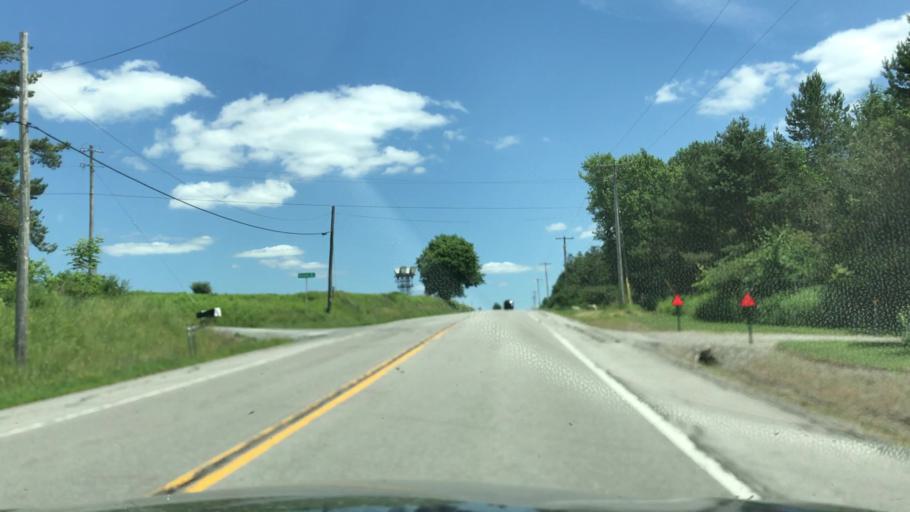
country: US
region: New York
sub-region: Wyoming County
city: Warsaw
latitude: 42.7482
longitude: -78.2346
